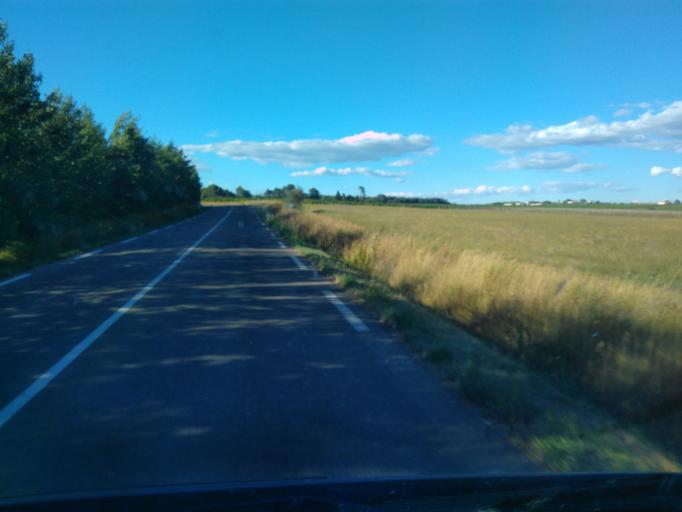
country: FR
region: Languedoc-Roussillon
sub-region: Departement du Gard
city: Vauvert
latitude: 43.6597
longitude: 4.2852
